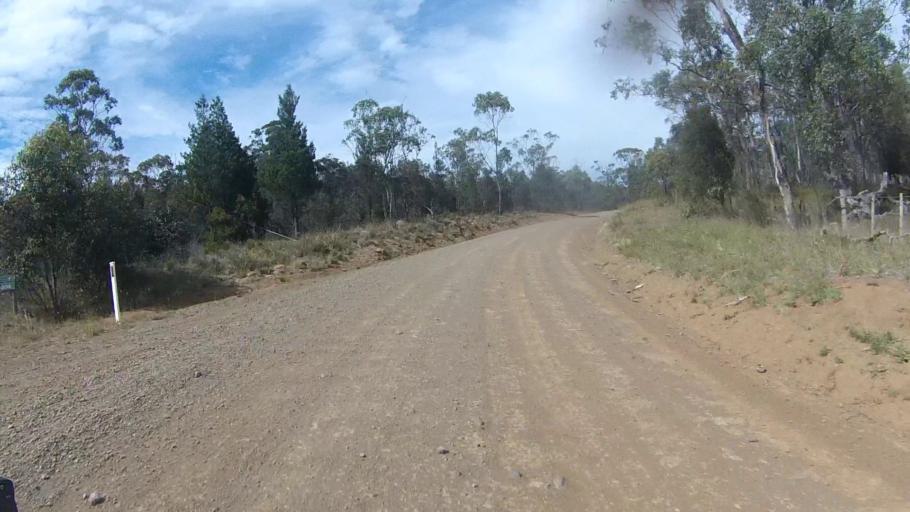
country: AU
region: Tasmania
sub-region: Sorell
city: Sorell
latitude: -42.6483
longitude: 147.8995
